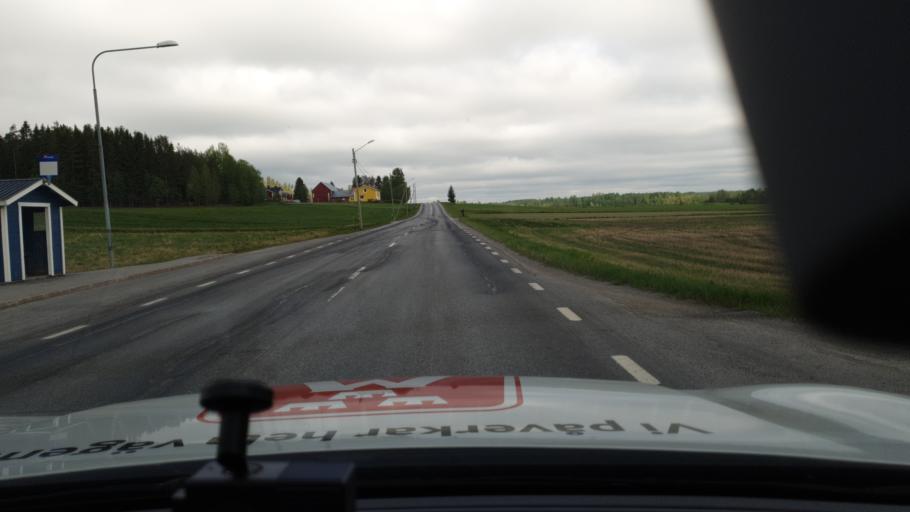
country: SE
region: Vaesterbotten
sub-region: Umea Kommun
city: Roback
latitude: 63.9151
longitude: 20.1964
